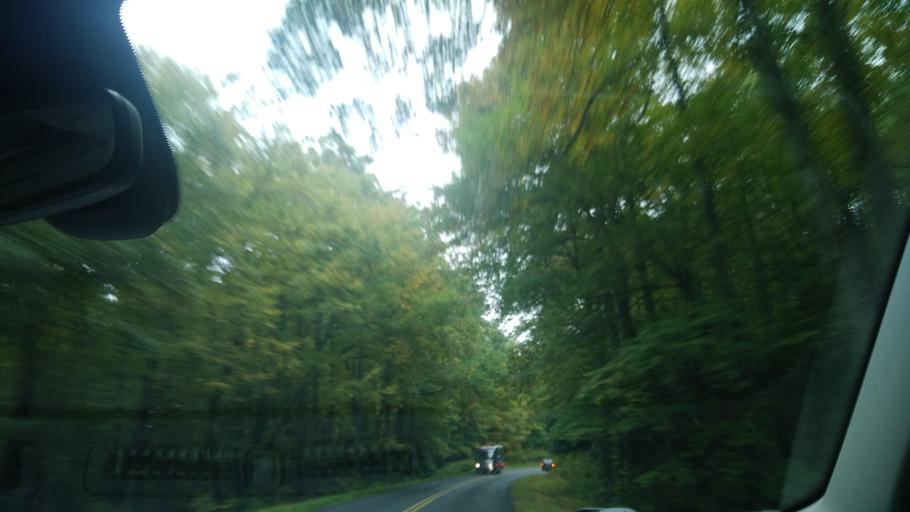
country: US
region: Virginia
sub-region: Carroll County
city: Cana
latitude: 36.6726
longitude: -80.6411
